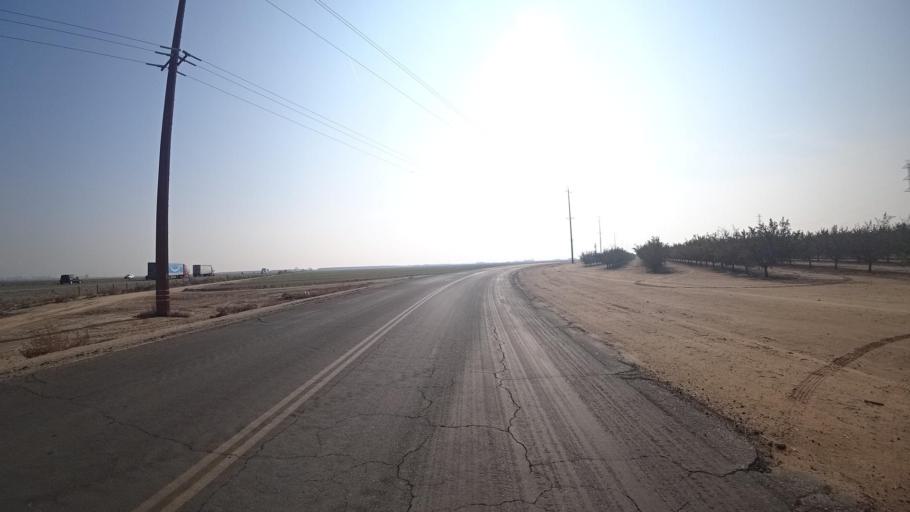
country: US
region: California
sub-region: Kern County
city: Buttonwillow
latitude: 35.4348
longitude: -119.4473
